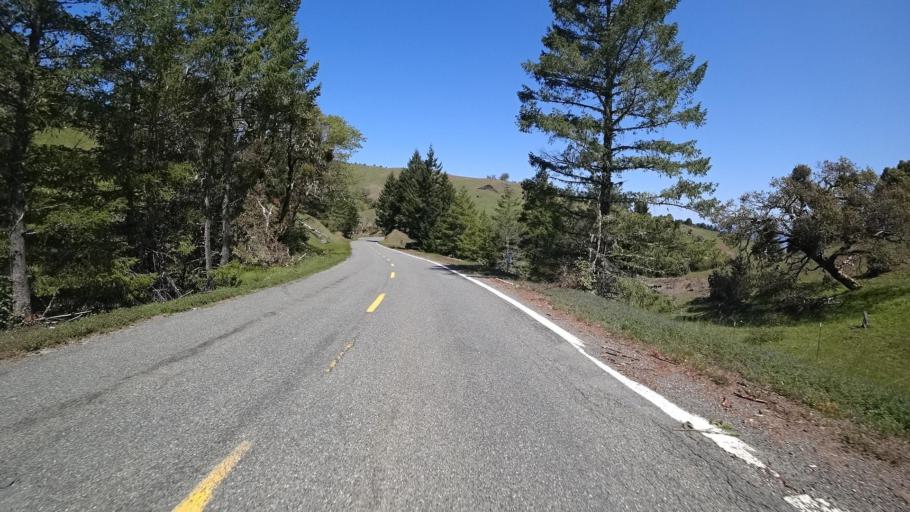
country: US
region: California
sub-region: Humboldt County
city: Redway
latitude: 40.1012
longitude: -123.6841
